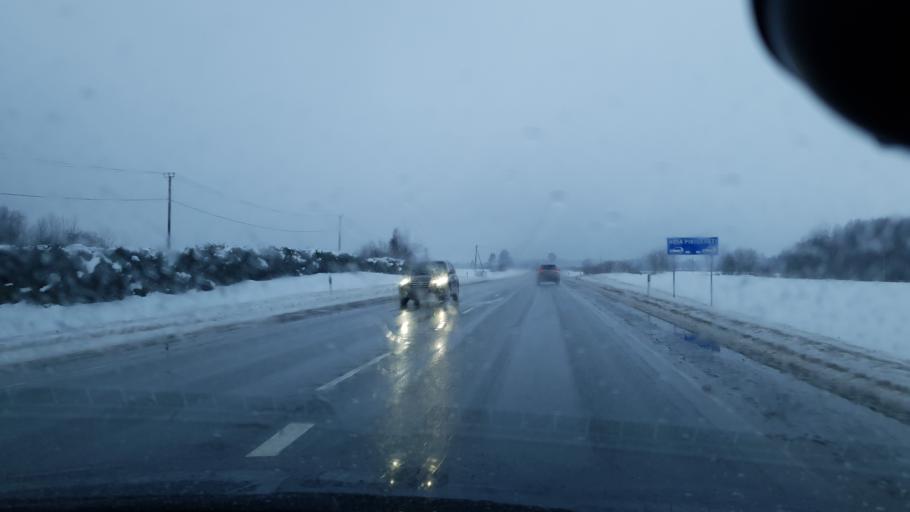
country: EE
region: Harju
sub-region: Anija vald
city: Kehra
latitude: 59.1660
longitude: 25.2677
